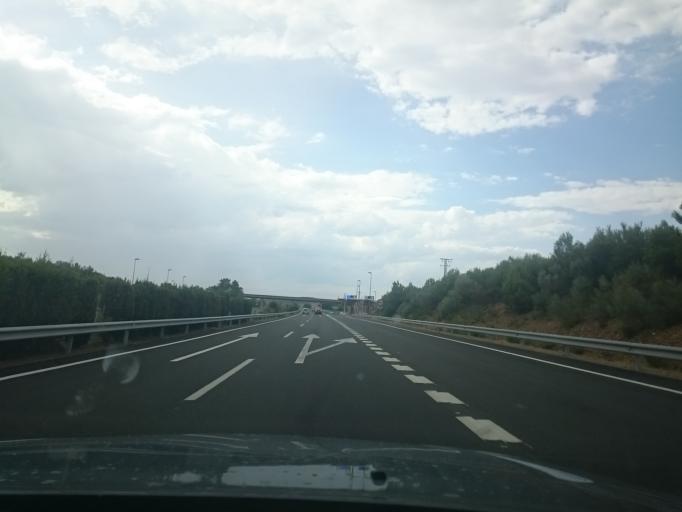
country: ES
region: Navarre
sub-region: Provincia de Navarra
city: Sartaguda
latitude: 42.3676
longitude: -2.0744
